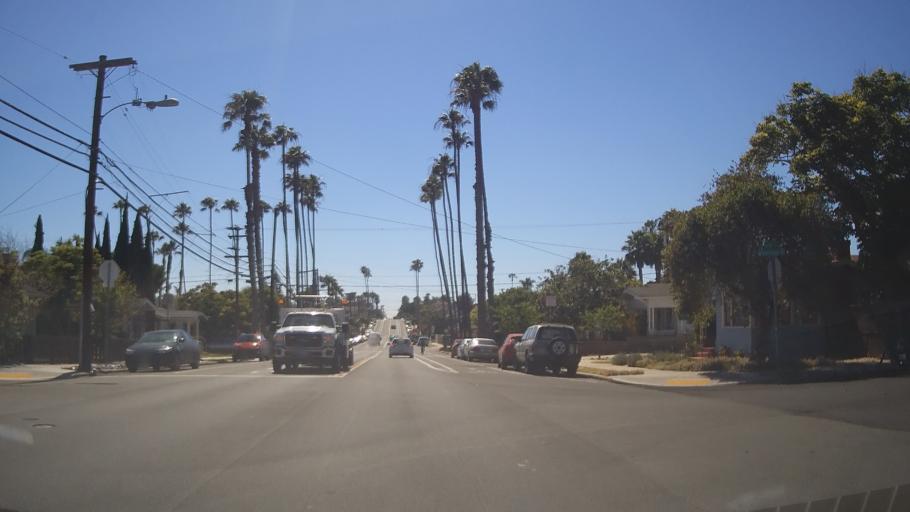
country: US
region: California
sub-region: San Diego County
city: San Diego
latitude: 32.7610
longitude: -117.1412
